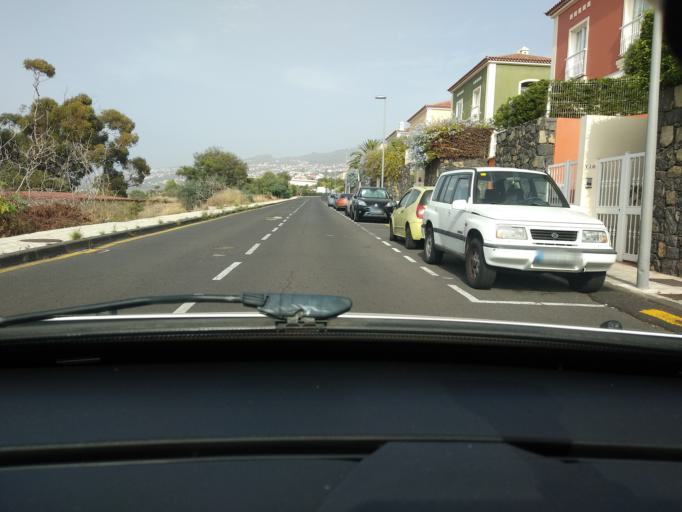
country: ES
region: Canary Islands
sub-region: Provincia de Santa Cruz de Tenerife
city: Santa Ursula
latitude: 28.4282
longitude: -16.4930
